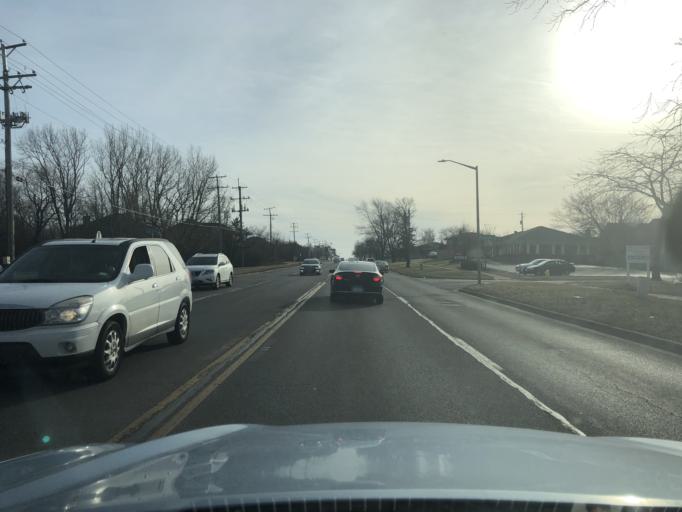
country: US
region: Illinois
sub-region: DuPage County
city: Glendale Heights
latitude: 41.9233
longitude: -88.0811
